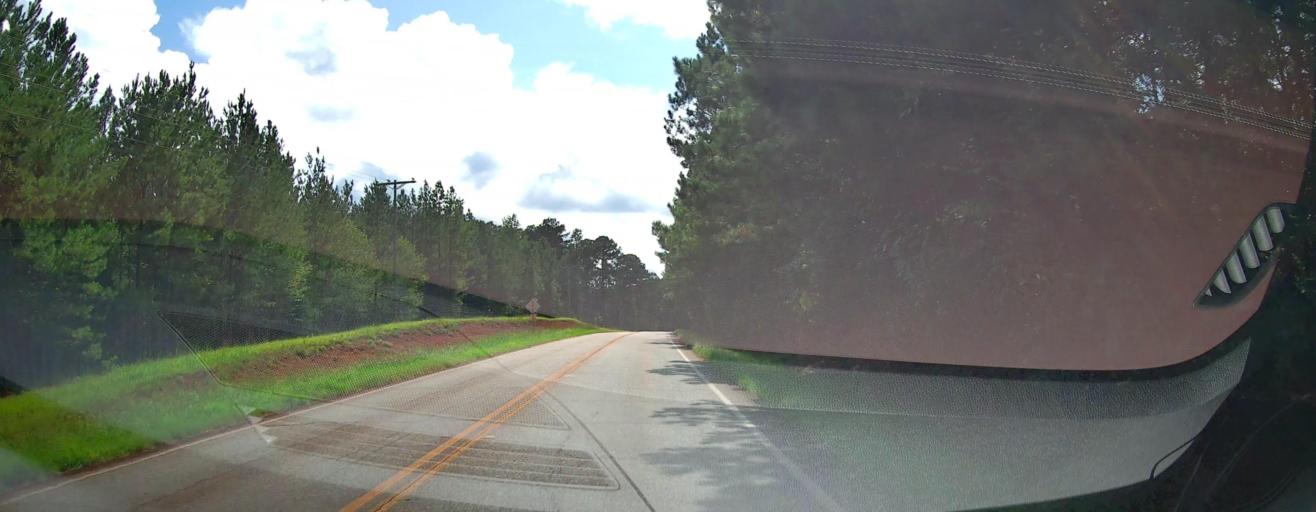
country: US
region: Georgia
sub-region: Crawford County
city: Roberta
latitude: 32.8751
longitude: -84.0316
